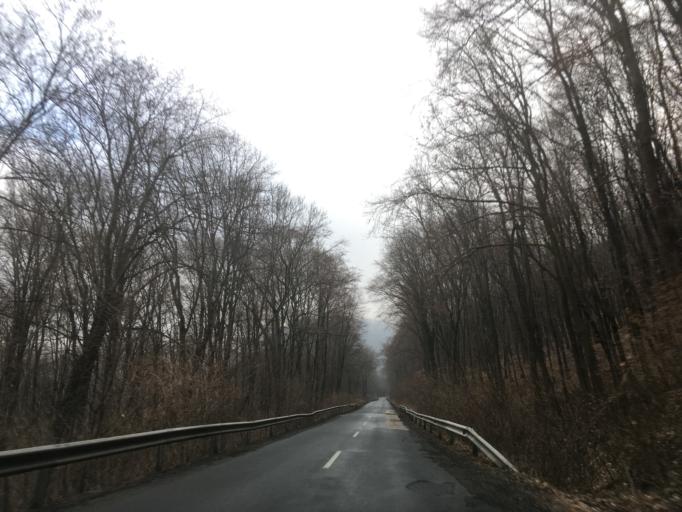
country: HU
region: Komarom-Esztergom
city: Kesztolc
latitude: 47.7243
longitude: 18.8393
